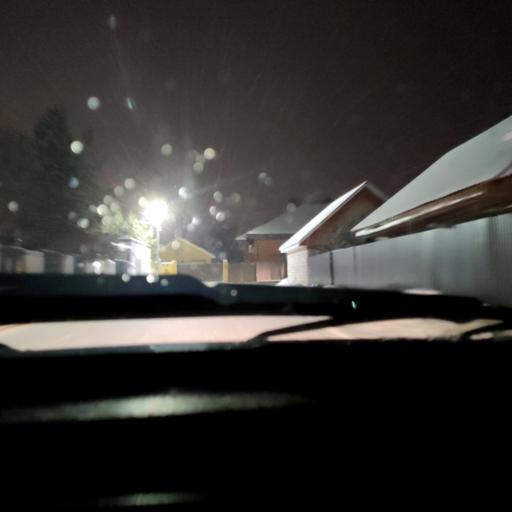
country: RU
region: Bashkortostan
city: Ufa
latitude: 54.7696
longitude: 55.9472
